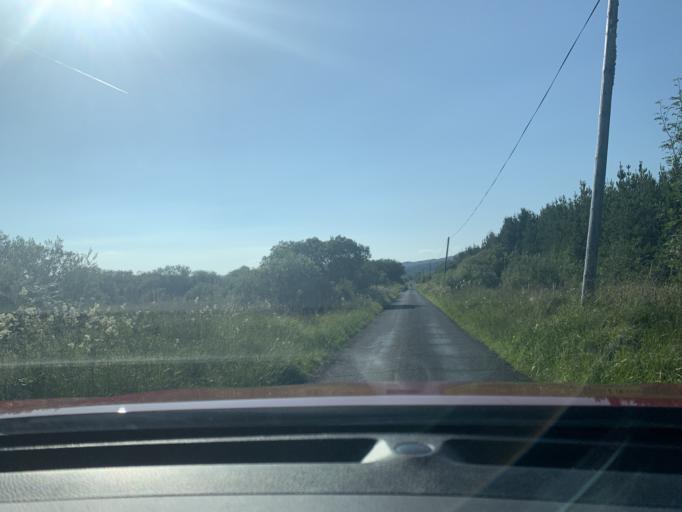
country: IE
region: Connaught
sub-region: Sligo
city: Tobercurry
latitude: 54.0759
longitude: -8.7887
